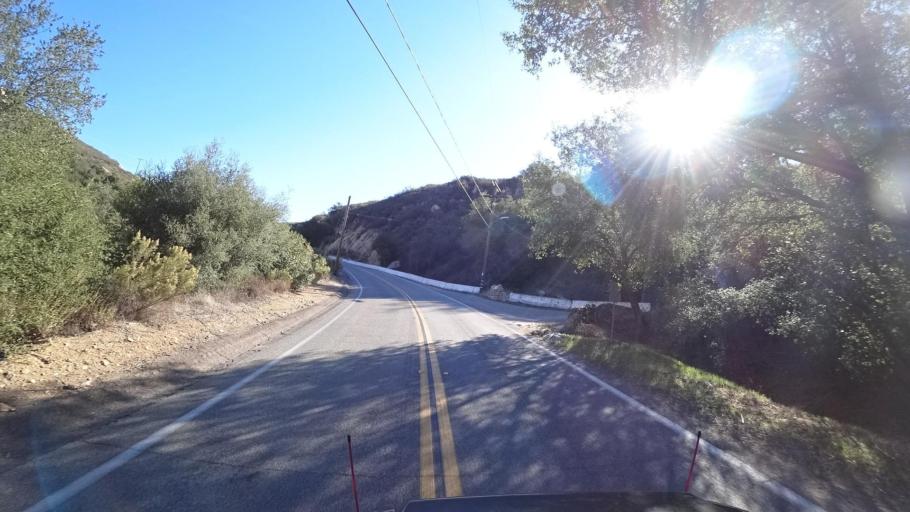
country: US
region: California
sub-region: San Diego County
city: Jamul
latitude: 32.6717
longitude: -116.7624
